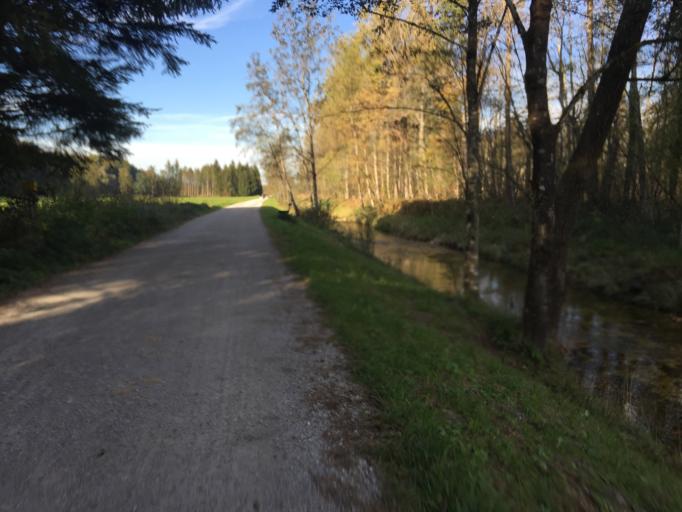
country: AT
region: Salzburg
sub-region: Politischer Bezirk Salzburg-Umgebung
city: Grodig
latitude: 47.7550
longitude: 12.9953
